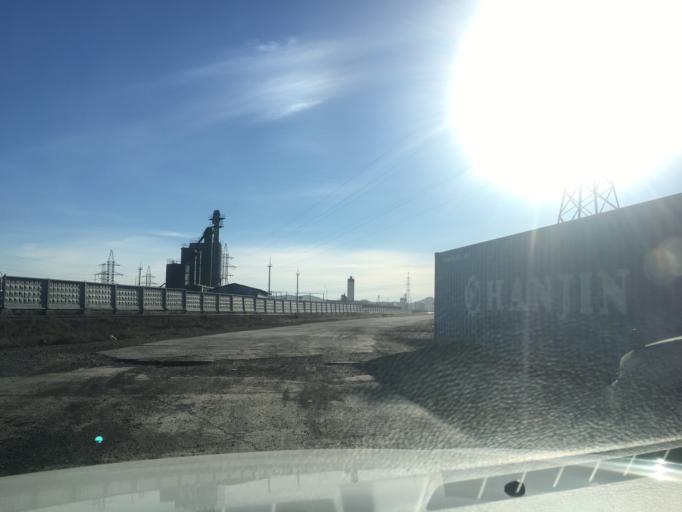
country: MN
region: Ulaanbaatar
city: Ulaanbaatar
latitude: 47.8996
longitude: 106.7354
